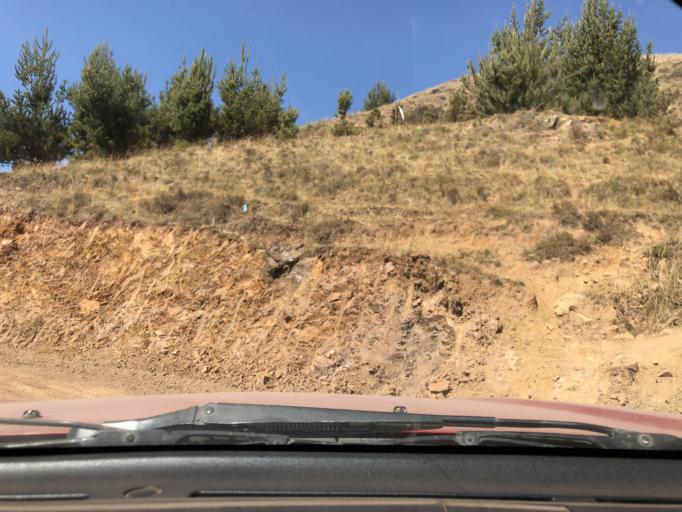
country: PE
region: Ayacucho
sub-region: Provincia de La Mar
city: Chilcas
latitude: -13.1827
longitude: -73.8449
